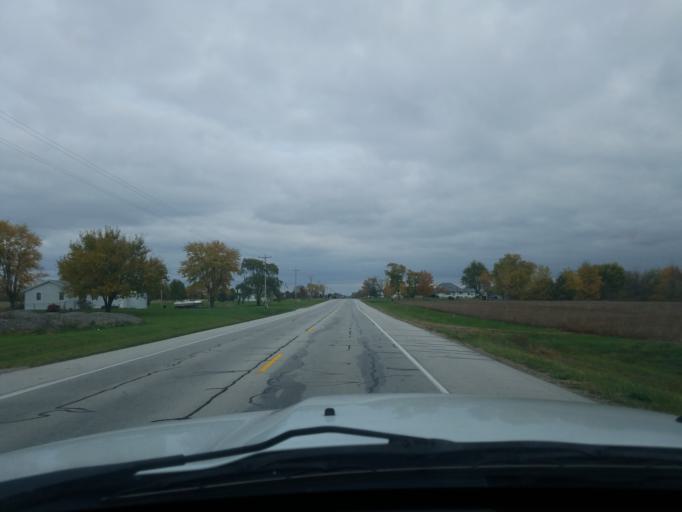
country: US
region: Indiana
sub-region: Johnson County
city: Franklin
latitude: 39.4954
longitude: -85.9208
